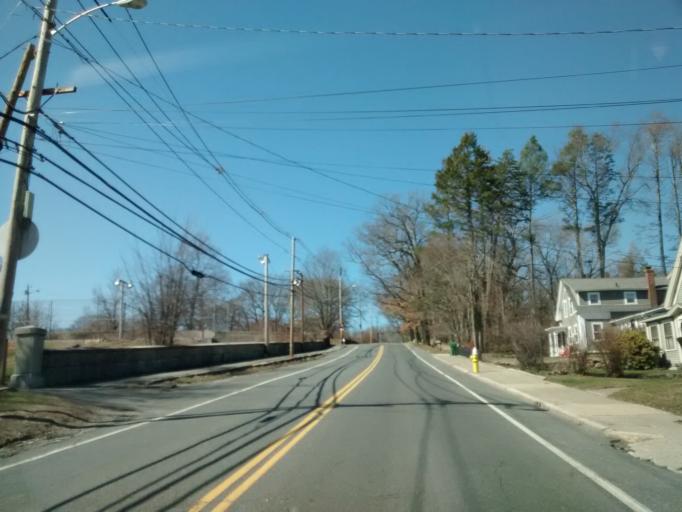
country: US
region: Massachusetts
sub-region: Worcester County
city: Whitinsville
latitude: 42.1123
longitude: -71.6664
